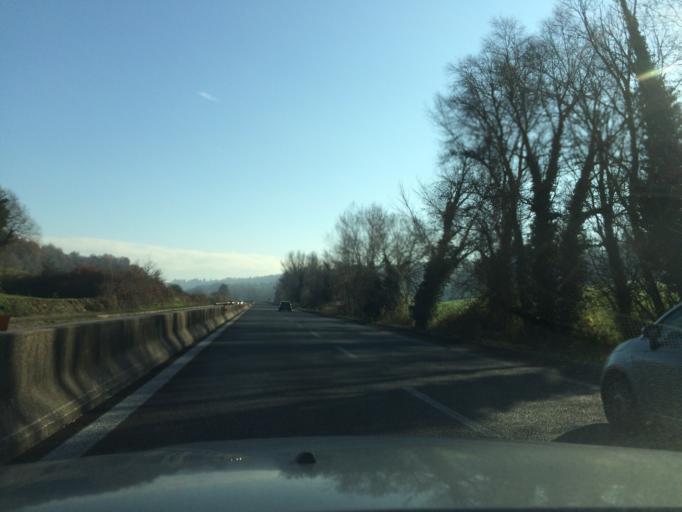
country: IT
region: Umbria
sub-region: Provincia di Perugia
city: Todi
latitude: 42.7631
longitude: 12.4544
